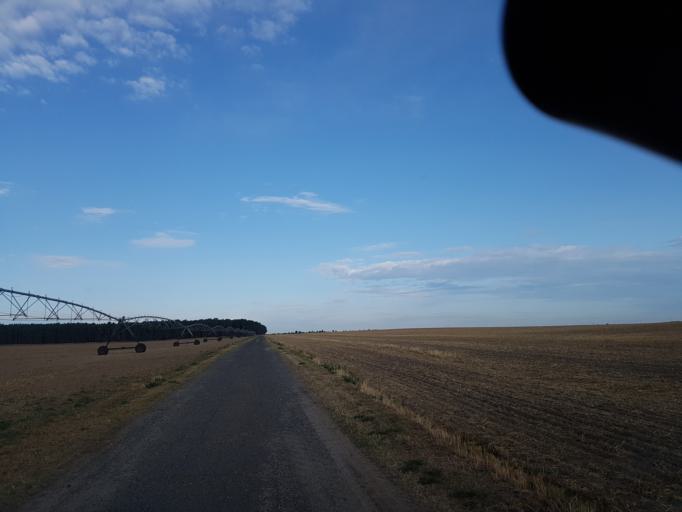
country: DE
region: Brandenburg
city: Niedergorsdorf
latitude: 51.9333
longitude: 13.0178
